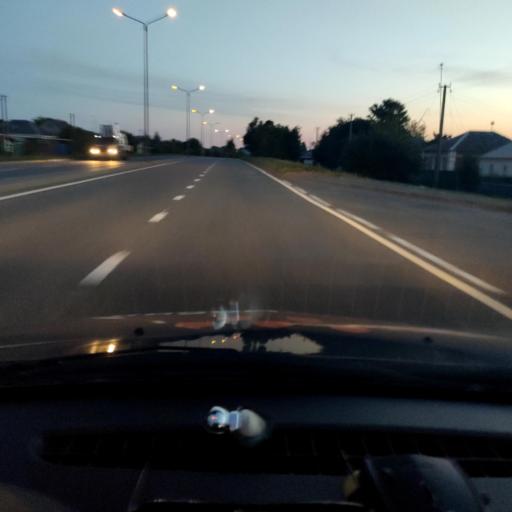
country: RU
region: Belgorod
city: Gubkin
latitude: 51.2725
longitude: 37.5829
